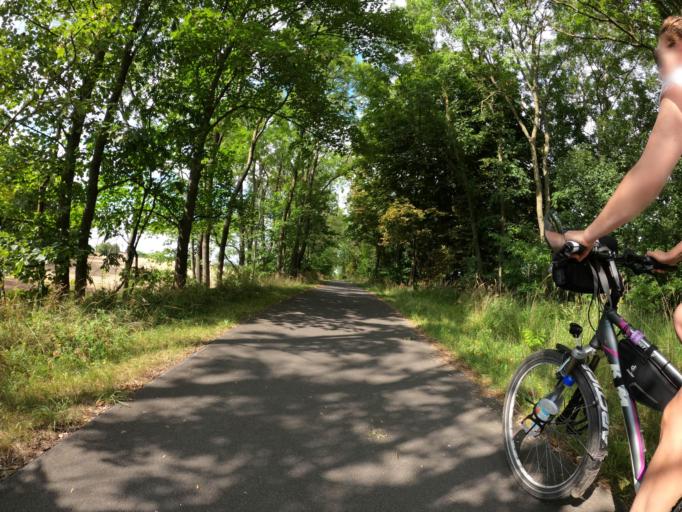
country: DE
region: Mecklenburg-Vorpommern
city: Woldegk
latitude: 53.3826
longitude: 13.5891
